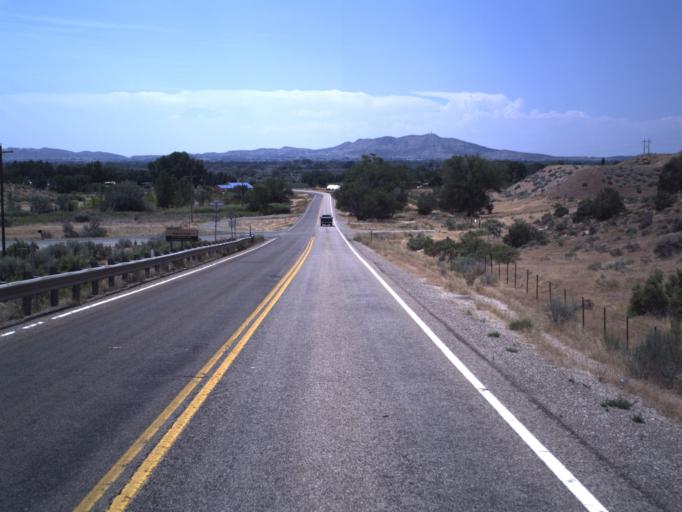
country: US
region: Utah
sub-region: Uintah County
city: Vernal
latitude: 40.5090
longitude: -109.5250
